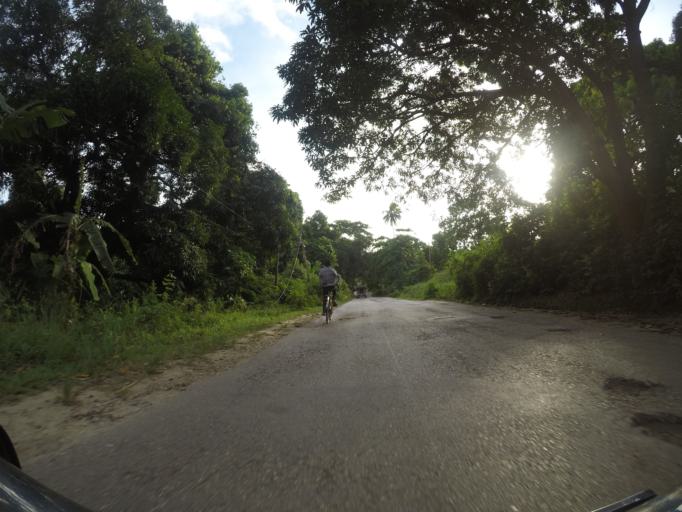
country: TZ
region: Pemba South
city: Chake Chake
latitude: -5.2722
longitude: 39.7711
